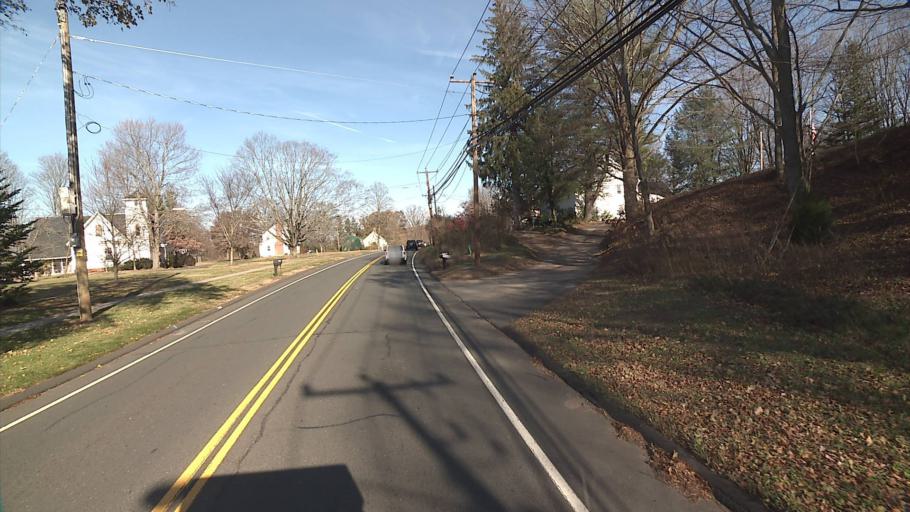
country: US
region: Connecticut
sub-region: Hartford County
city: Glastonbury Center
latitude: 41.6710
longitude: -72.6012
